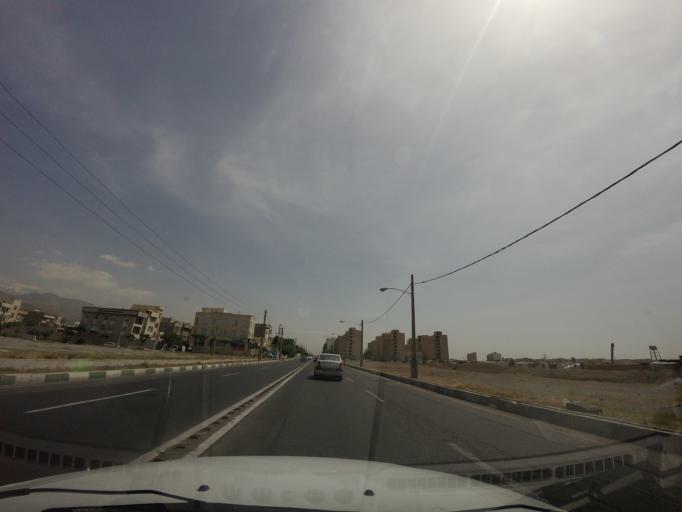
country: IR
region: Tehran
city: Shahr-e Qods
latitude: 35.7452
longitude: 51.2423
